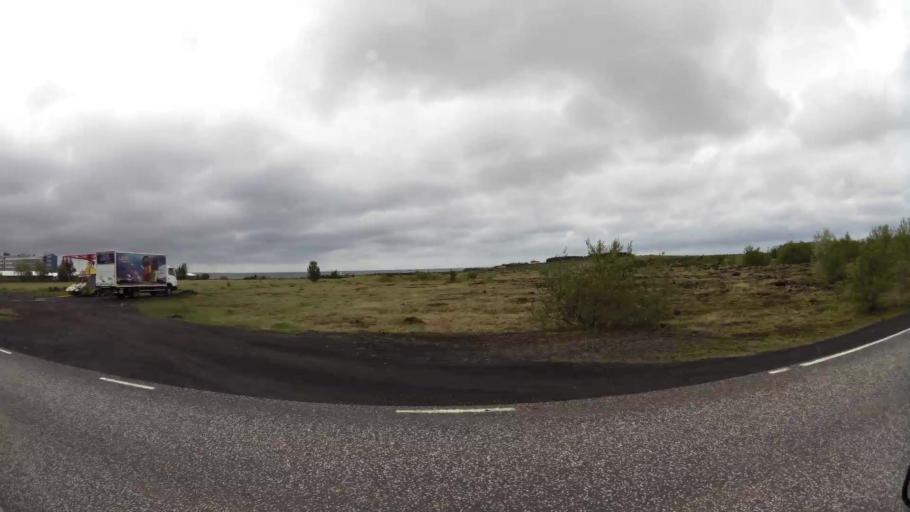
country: IS
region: Capital Region
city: Hafnarfjoerdur
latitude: 64.0829
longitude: -21.9690
